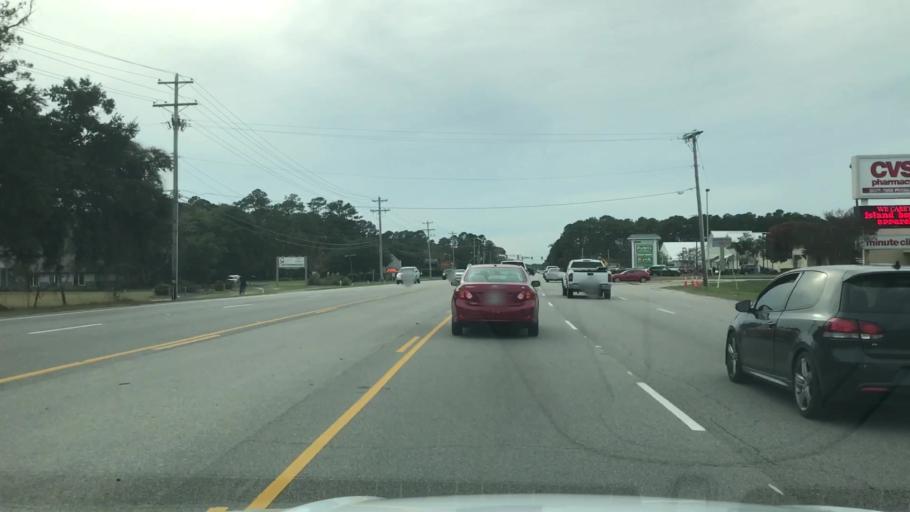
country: US
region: South Carolina
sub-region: Georgetown County
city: Murrells Inlet
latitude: 33.4375
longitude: -79.1294
